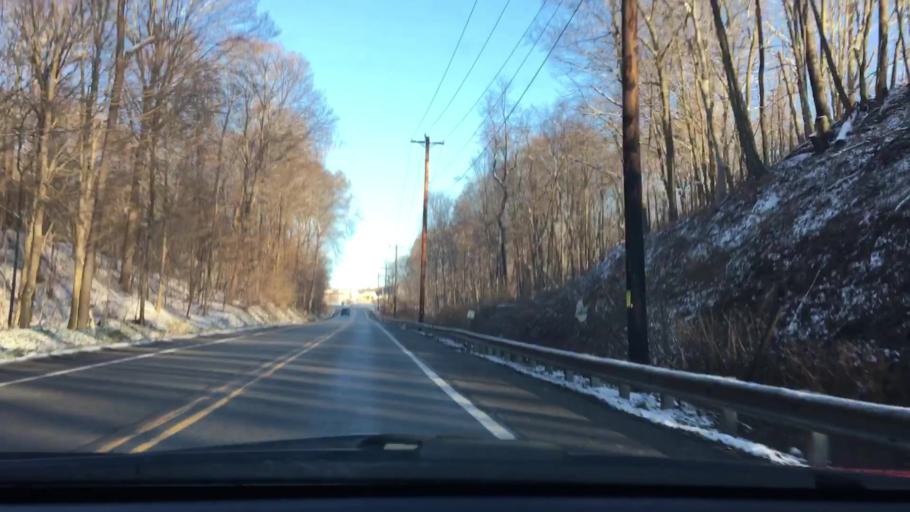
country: US
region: Pennsylvania
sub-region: Allegheny County
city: Glassport
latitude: 40.3336
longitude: -79.9108
